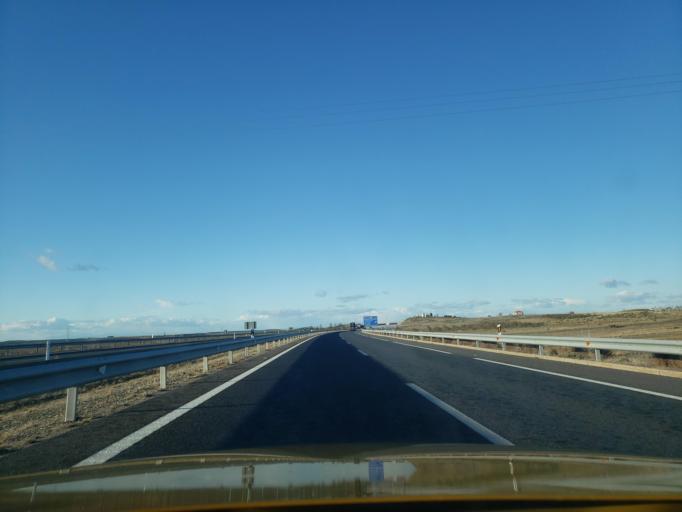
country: ES
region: Castille-La Mancha
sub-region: Province of Toledo
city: Villaminaya
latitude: 39.7437
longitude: -3.8627
